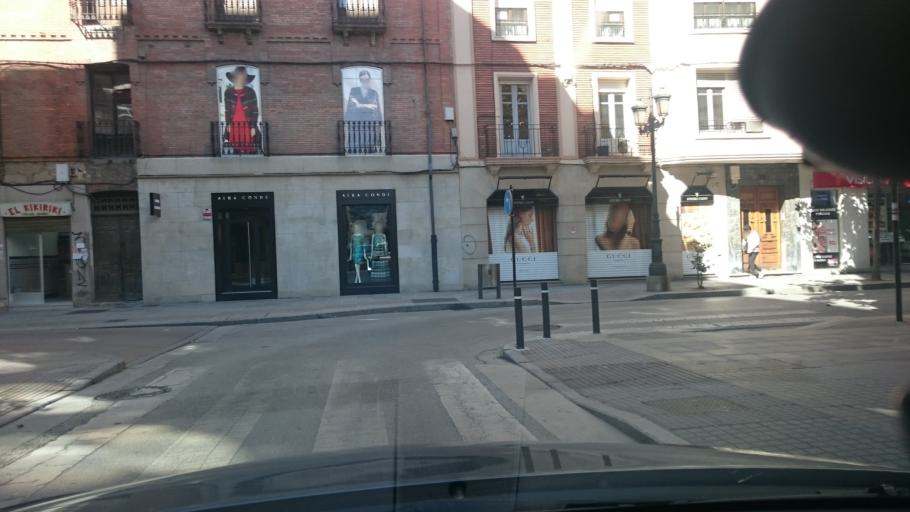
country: ES
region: Castille and Leon
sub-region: Provincia de Leon
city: Ponferrada
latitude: 42.5474
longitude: -6.6011
